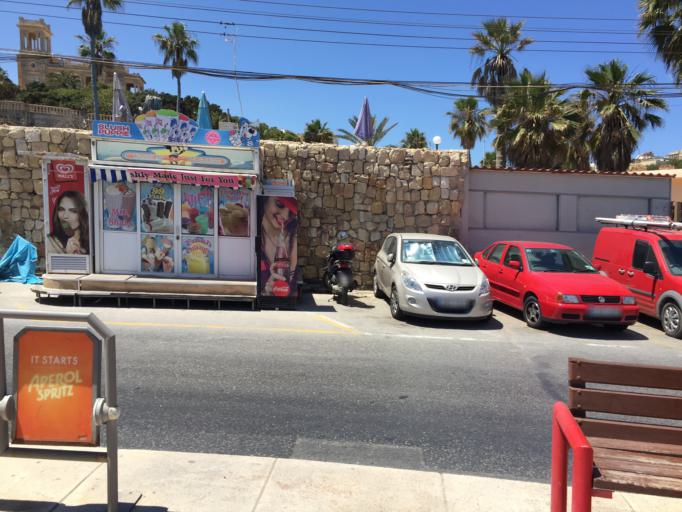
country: MT
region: Saint Julian
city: San Giljan
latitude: 35.9261
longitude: 14.4874
